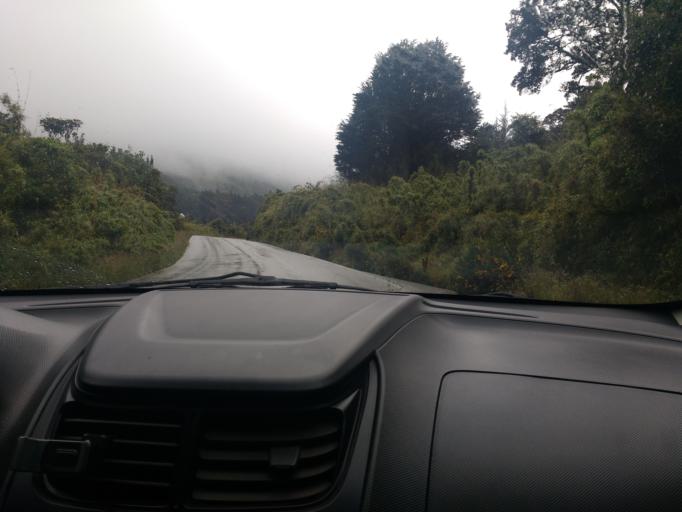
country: CO
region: Bogota D.C.
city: Bogota
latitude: 4.5872
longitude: -74.0449
